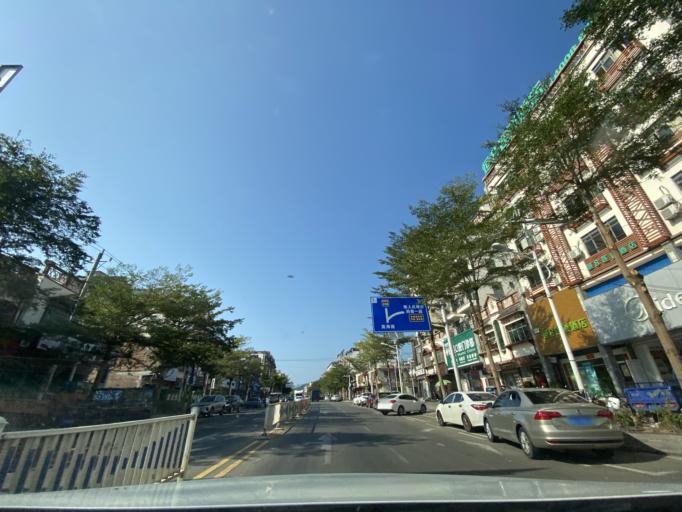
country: CN
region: Hainan
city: Yingzhou
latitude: 18.4274
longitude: 109.8546
